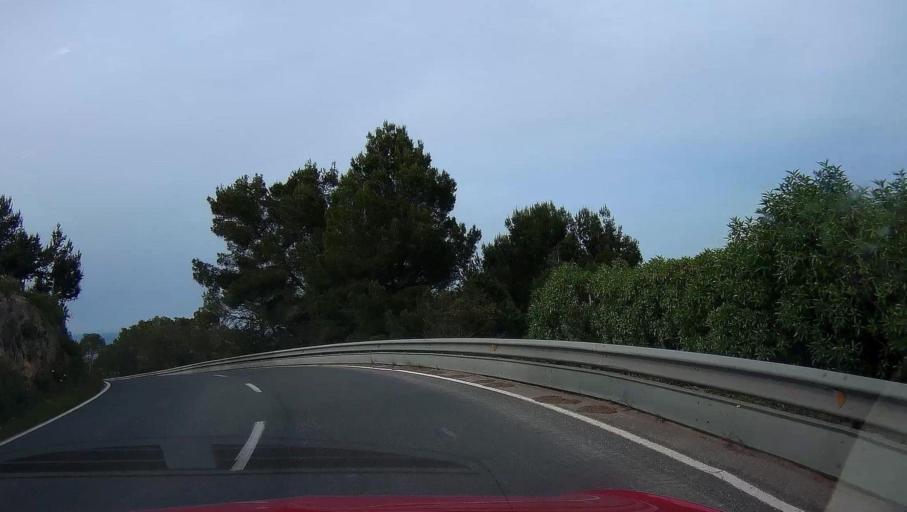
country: ES
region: Balearic Islands
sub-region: Illes Balears
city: Sant Joan de Labritja
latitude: 39.0791
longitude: 1.5025
